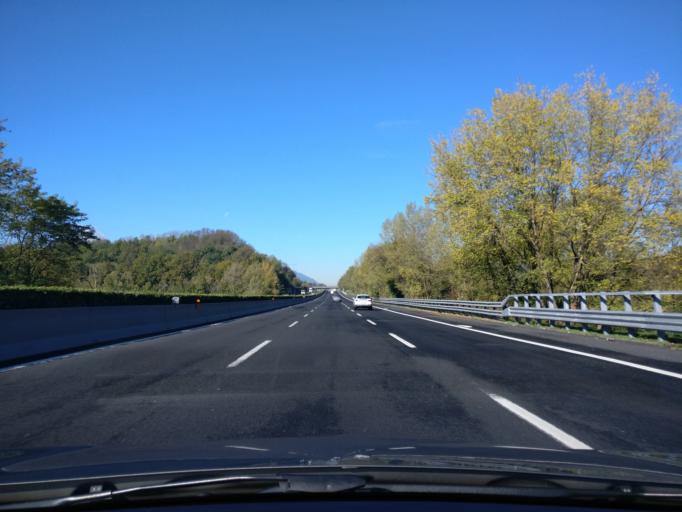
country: IT
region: Latium
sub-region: Provincia di Frosinone
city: Pofi
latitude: 41.5610
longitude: 13.4056
